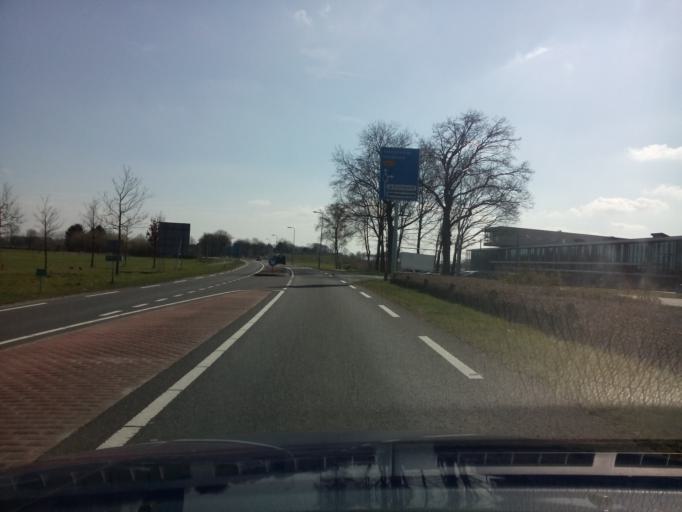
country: NL
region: Drenthe
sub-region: Gemeente Coevorden
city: Coevorden
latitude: 52.6501
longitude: 6.7536
